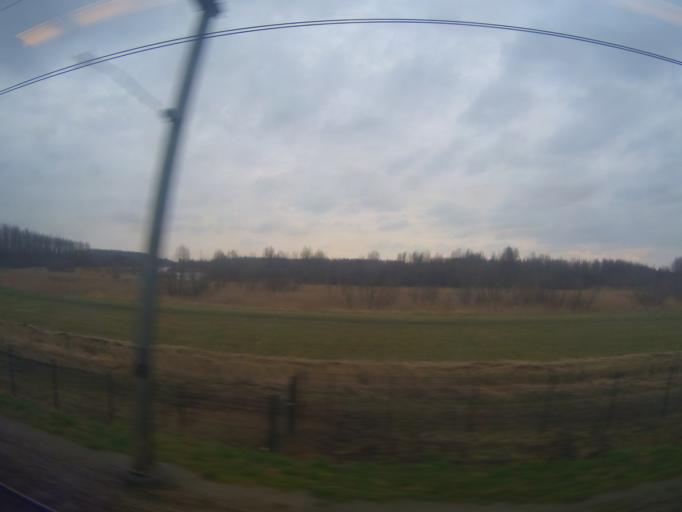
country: NL
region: South Holland
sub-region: Gemeente Pijnacker-Nootdorp
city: Pijnacker
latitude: 52.0505
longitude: 4.4377
